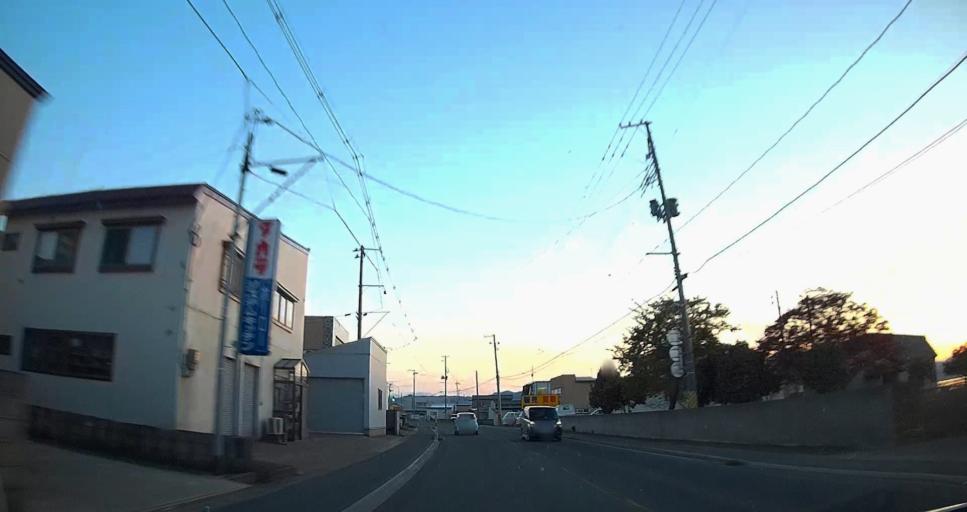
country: JP
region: Aomori
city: Misawa
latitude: 40.8722
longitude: 141.1336
